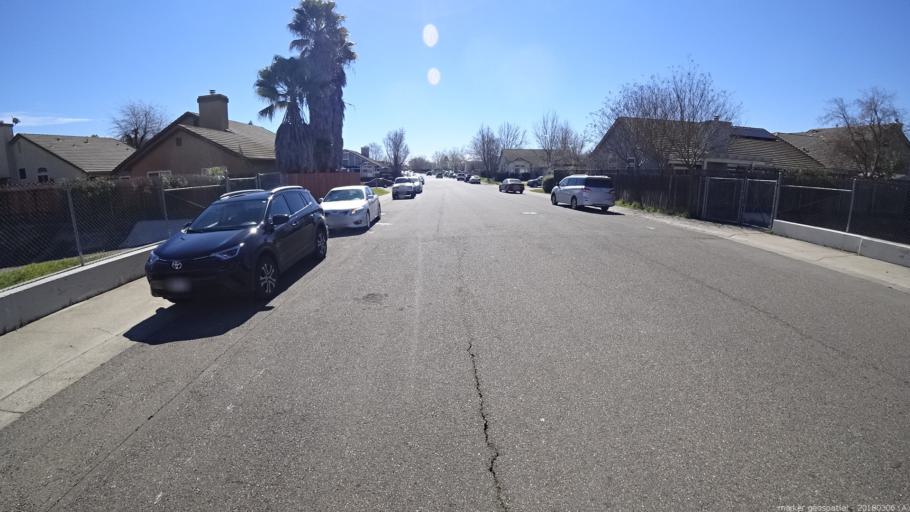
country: US
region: California
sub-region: Sacramento County
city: Vineyard
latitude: 38.4631
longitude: -121.3642
